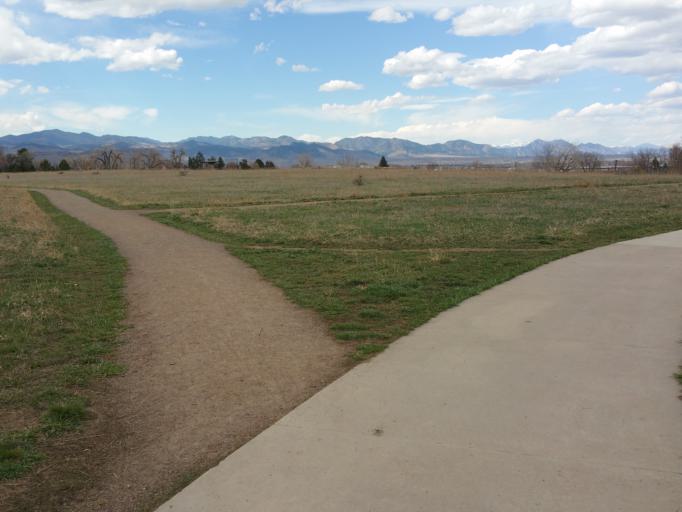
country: US
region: Colorado
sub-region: Jefferson County
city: Wheat Ridge
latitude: 39.7600
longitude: -105.0996
